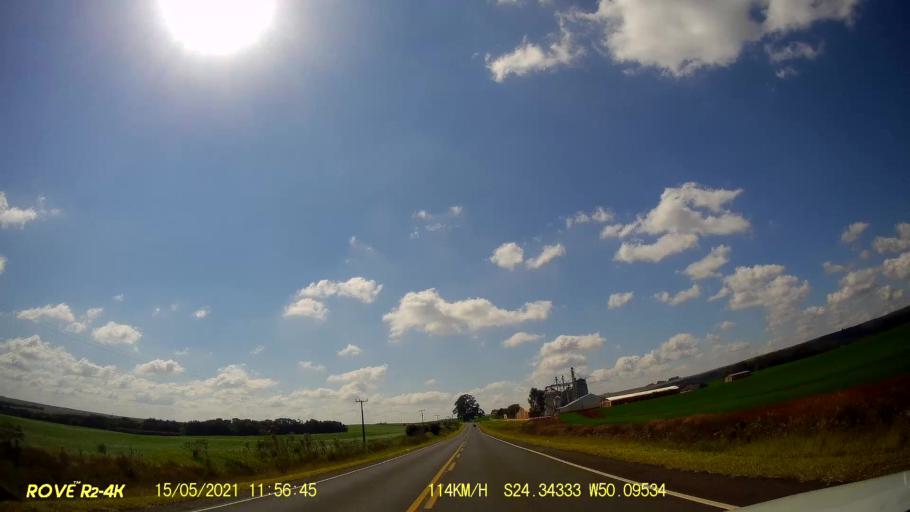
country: BR
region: Parana
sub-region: Pirai Do Sul
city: Pirai do Sul
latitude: -24.3434
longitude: -50.0954
